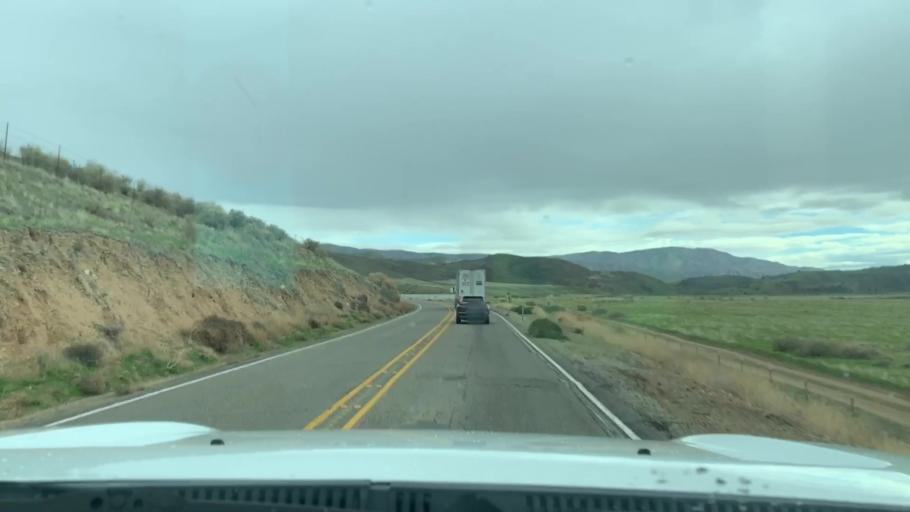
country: US
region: California
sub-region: Santa Barbara County
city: Los Olivos
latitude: 35.0604
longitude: -119.9570
